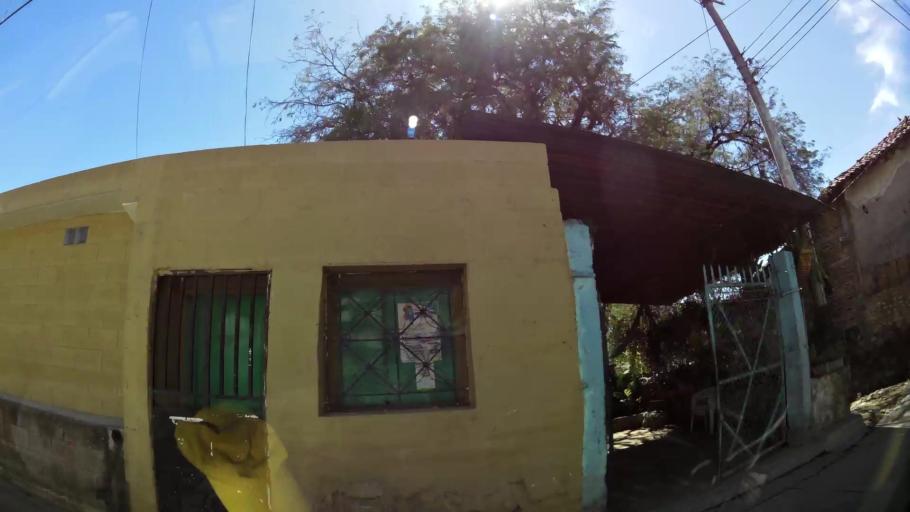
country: SV
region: San Salvador
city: Apopa
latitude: 13.8090
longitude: -89.1734
